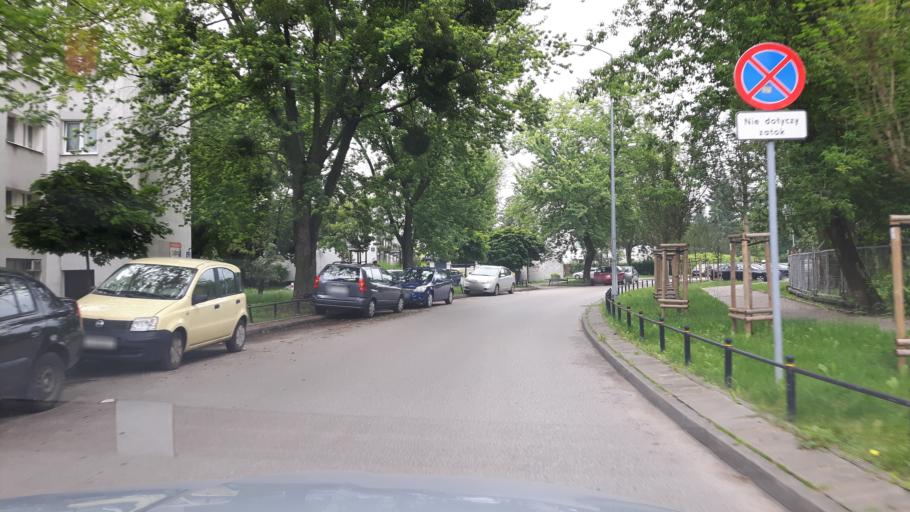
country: PL
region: Masovian Voivodeship
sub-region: Warszawa
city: Zoliborz
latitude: 52.2631
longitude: 20.9656
